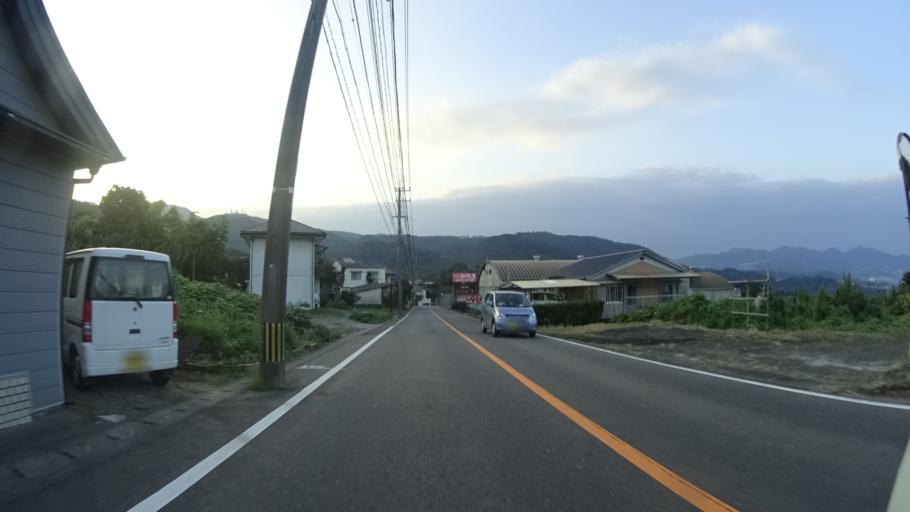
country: JP
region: Oita
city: Beppu
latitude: 33.3212
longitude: 131.4799
